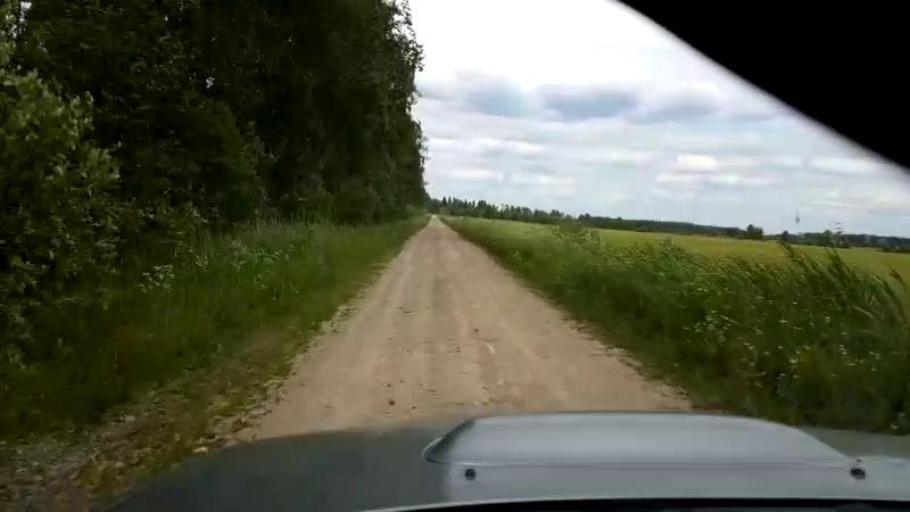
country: EE
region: Paernumaa
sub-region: Sauga vald
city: Sauga
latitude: 58.4950
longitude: 24.5814
